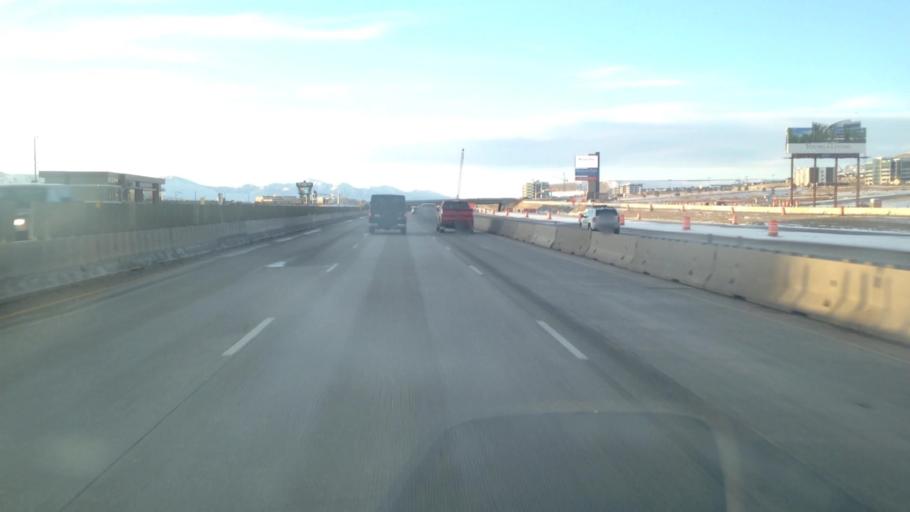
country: US
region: Utah
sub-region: Utah County
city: Lehi
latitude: 40.4200
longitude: -111.8773
